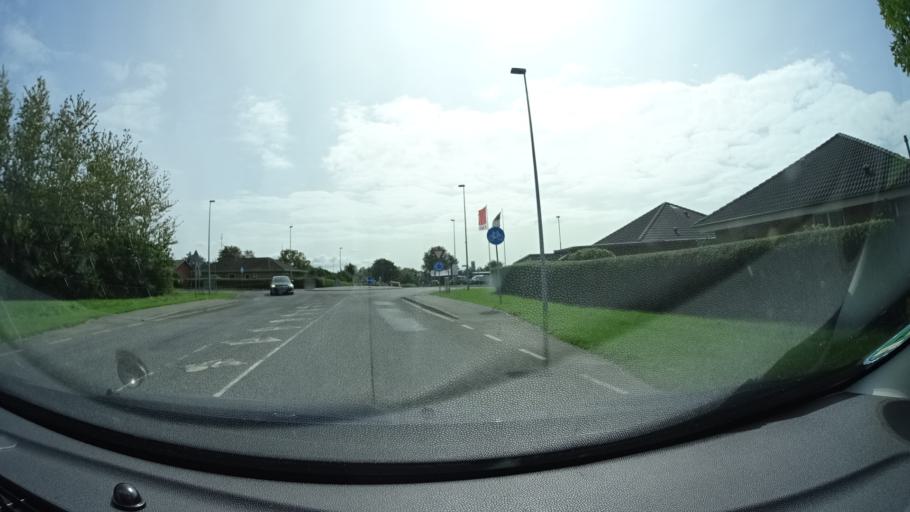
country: DE
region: Schleswig-Holstein
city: Rodenas
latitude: 54.9632
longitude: 8.7036
